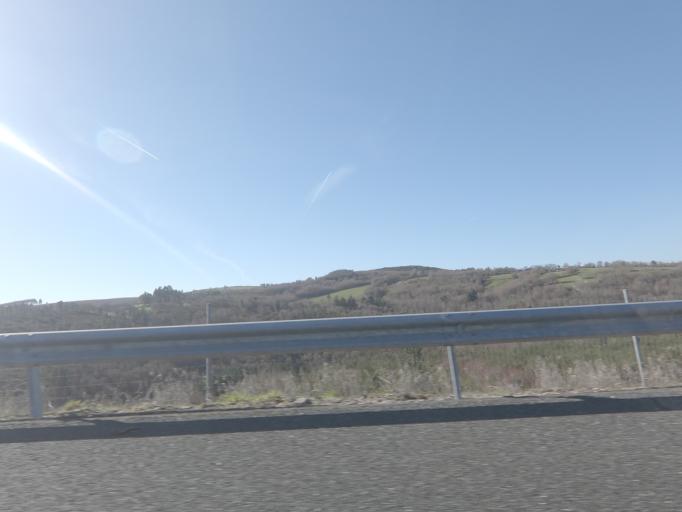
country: ES
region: Galicia
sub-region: Provincia de Pontevedra
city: Lalin
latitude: 42.6015
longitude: -8.0958
